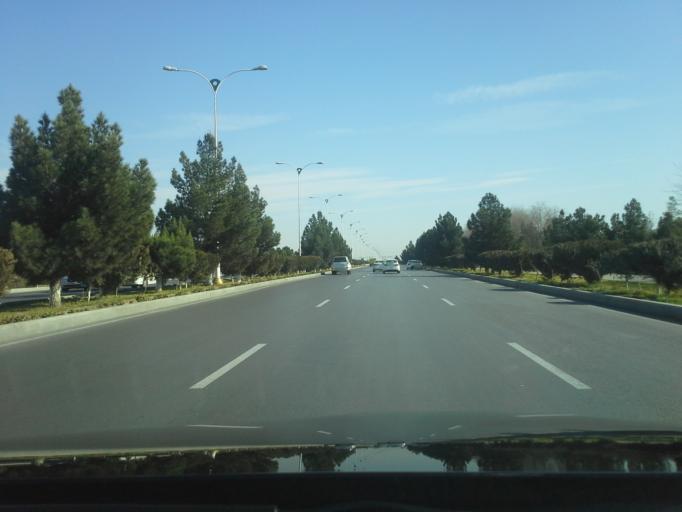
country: TM
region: Ahal
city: Annau
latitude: 37.9179
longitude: 58.4604
